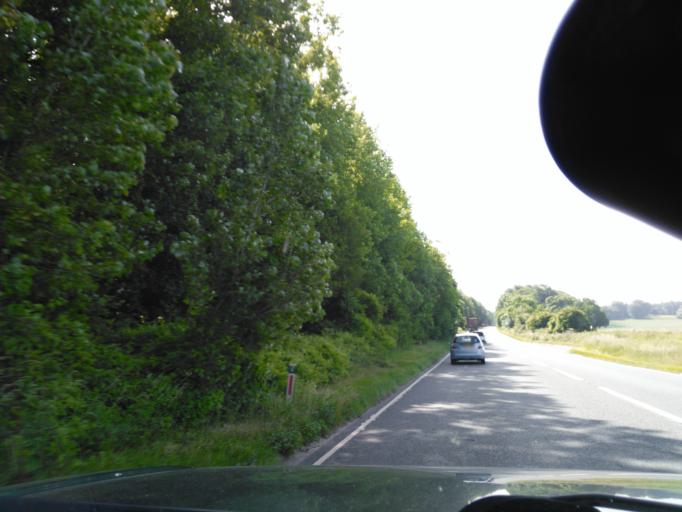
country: GB
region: England
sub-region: Wiltshire
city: Whiteparish
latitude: 51.0160
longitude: -1.6870
